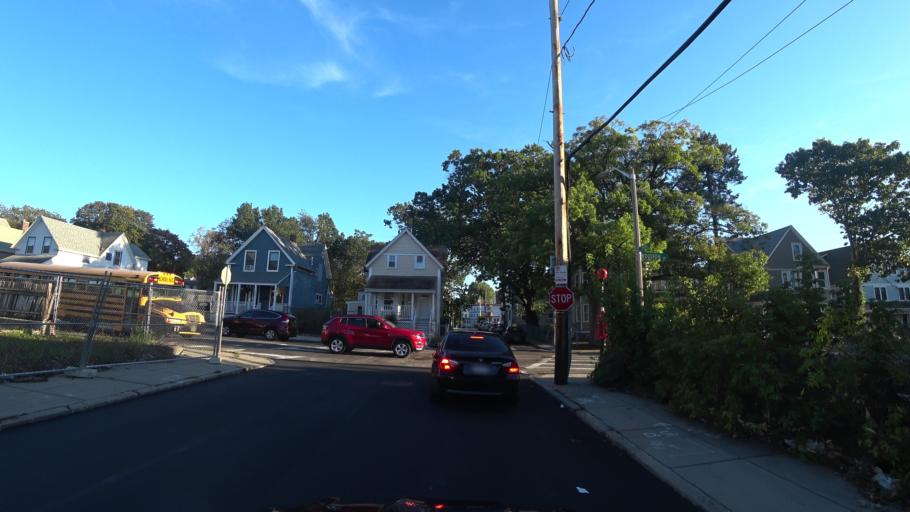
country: US
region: Massachusetts
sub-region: Norfolk County
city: Milton
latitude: 42.2875
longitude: -71.0835
